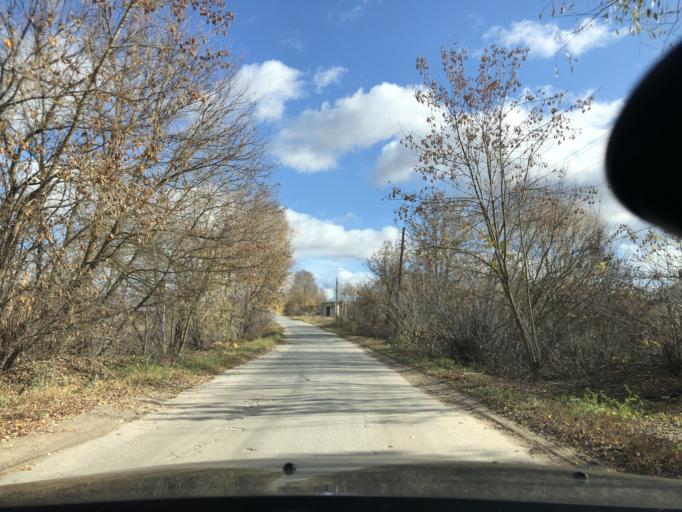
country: RU
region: Tula
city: Gorelki
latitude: 54.2950
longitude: 37.5612
